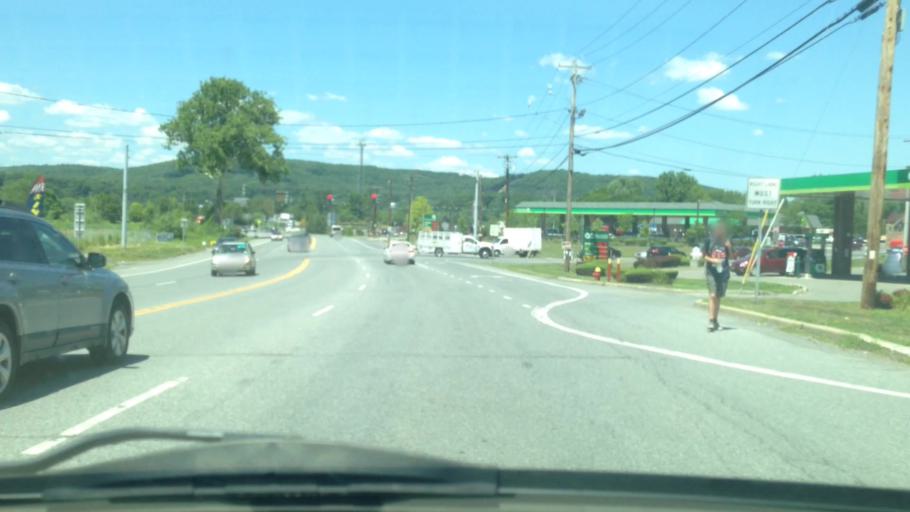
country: US
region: New York
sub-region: Ulster County
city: Kingston
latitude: 41.9401
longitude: -74.0270
